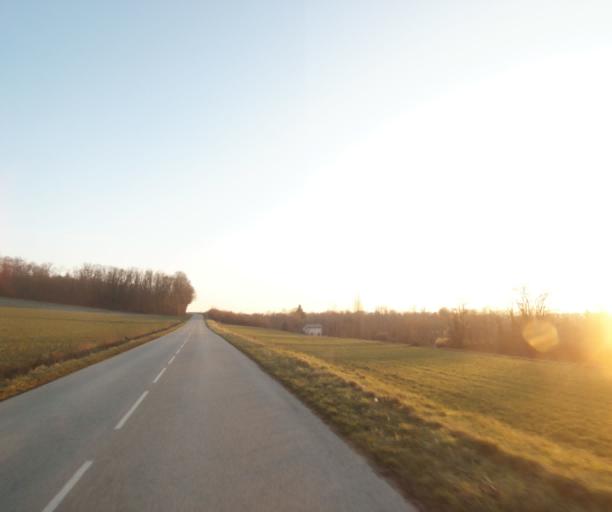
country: FR
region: Champagne-Ardenne
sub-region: Departement de la Haute-Marne
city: Bienville
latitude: 48.5932
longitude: 5.0416
